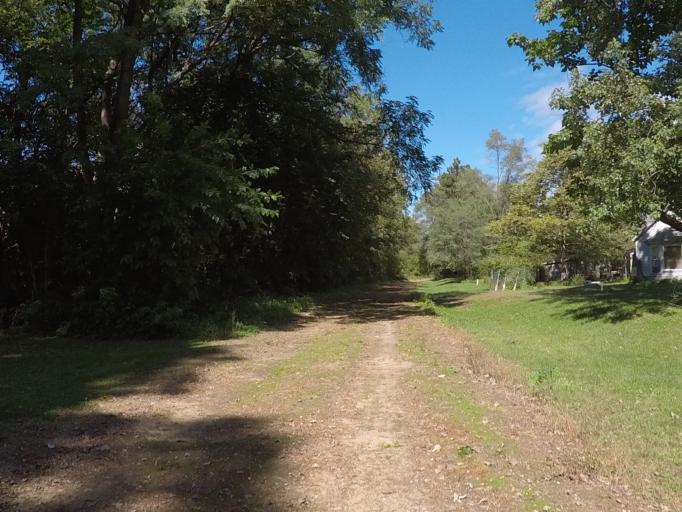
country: US
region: Wisconsin
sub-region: Richland County
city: Richland Center
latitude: 43.2202
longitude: -90.2945
